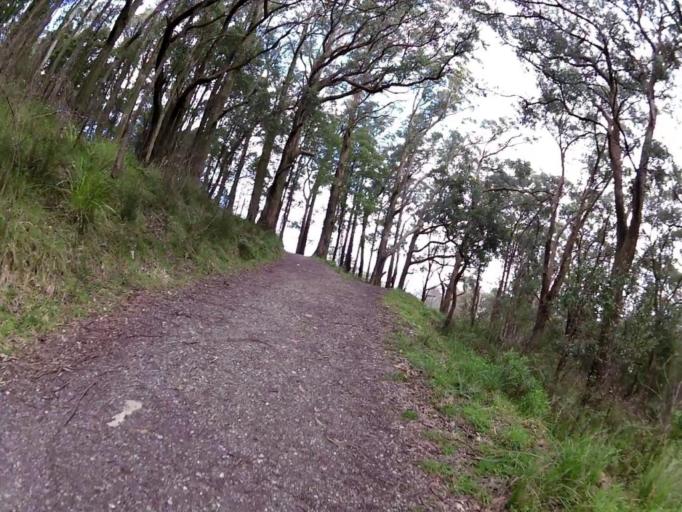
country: AU
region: Victoria
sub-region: Yarra Ranges
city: Montrose
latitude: -37.8366
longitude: 145.3466
